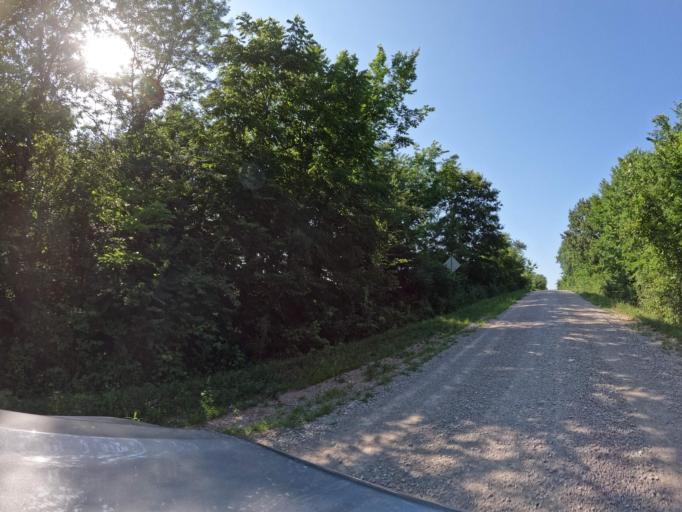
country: US
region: Iowa
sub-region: Appanoose County
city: Centerville
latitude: 40.7344
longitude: -93.0206
